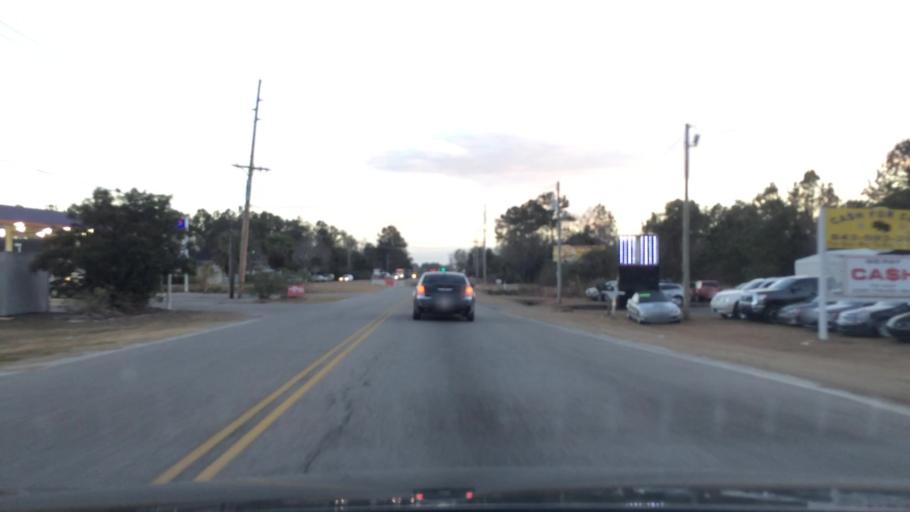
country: US
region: South Carolina
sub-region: Horry County
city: Red Hill
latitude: 33.8040
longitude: -79.0185
